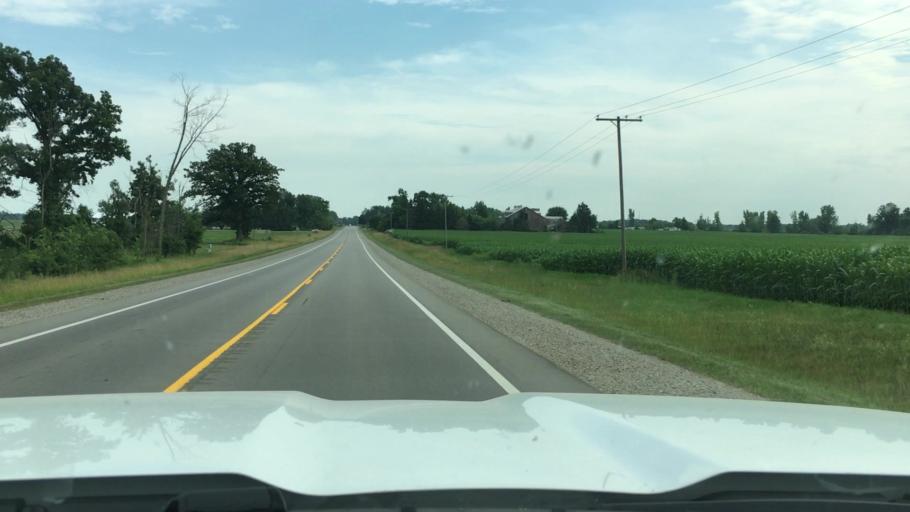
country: US
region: Michigan
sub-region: Sanilac County
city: Marlette
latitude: 43.3558
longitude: -83.0850
